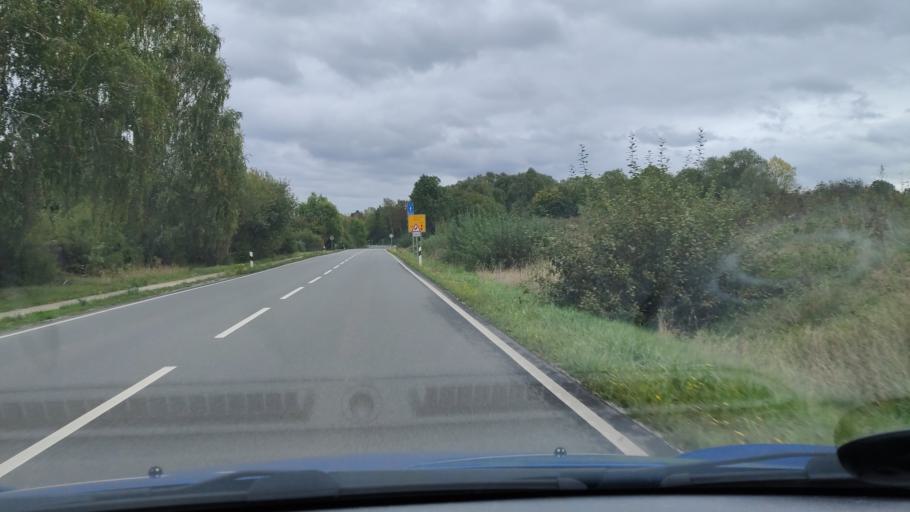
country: DE
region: Lower Saxony
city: Garbsen
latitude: 52.4043
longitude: 9.5304
